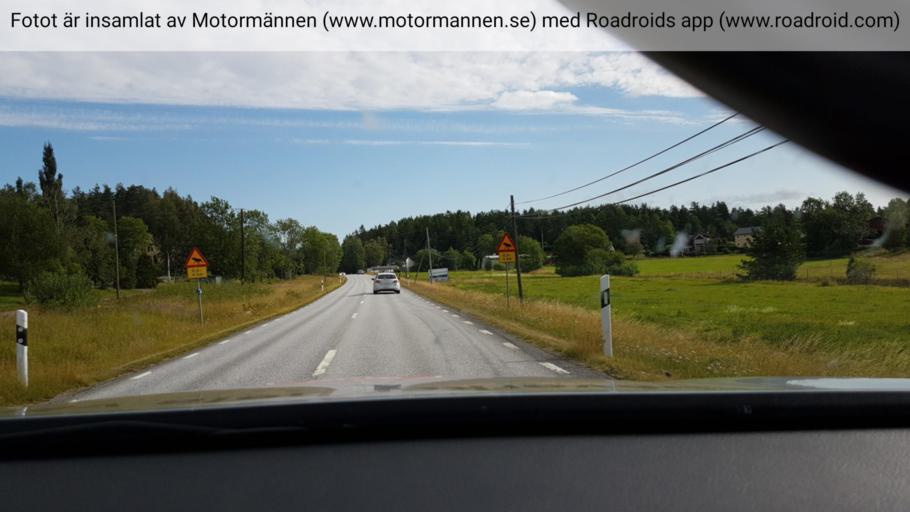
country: SE
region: Stockholm
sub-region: Vaxholms Kommun
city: Resaro
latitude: 59.5296
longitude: 18.4325
